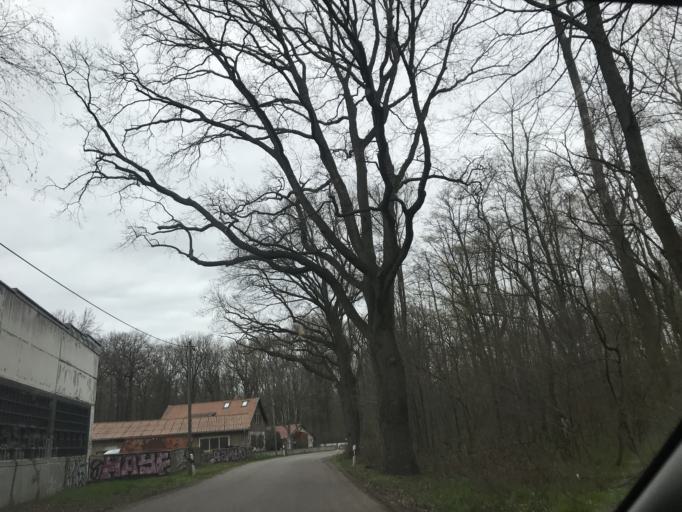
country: DE
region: Saxony
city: Schkeuditz
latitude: 51.3661
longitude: 12.2562
